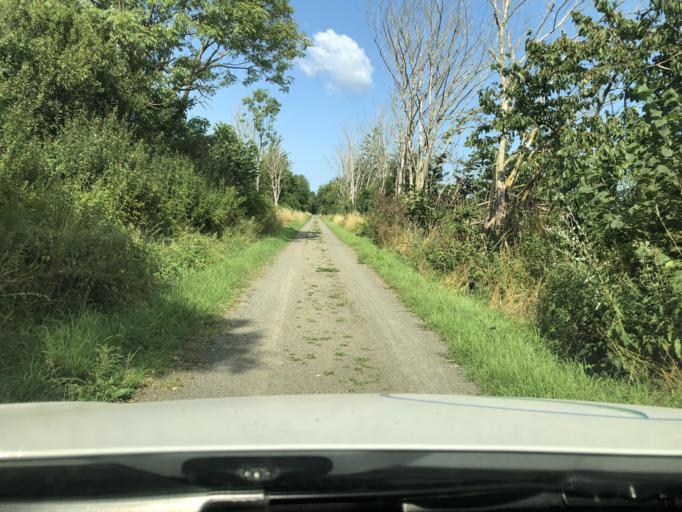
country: SE
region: Skane
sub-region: Kristianstads Kommun
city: Degeberga
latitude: 55.7717
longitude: 14.1583
